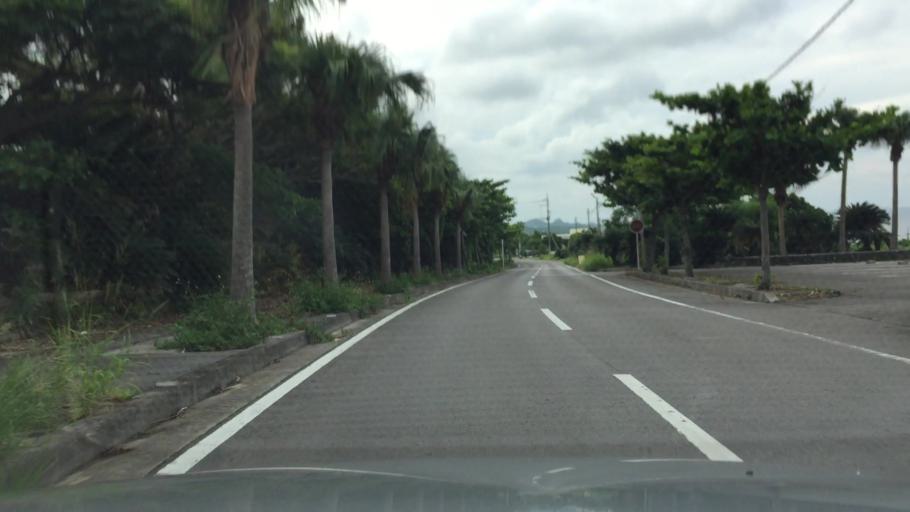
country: JP
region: Okinawa
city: Ishigaki
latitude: 24.4467
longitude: 124.1709
